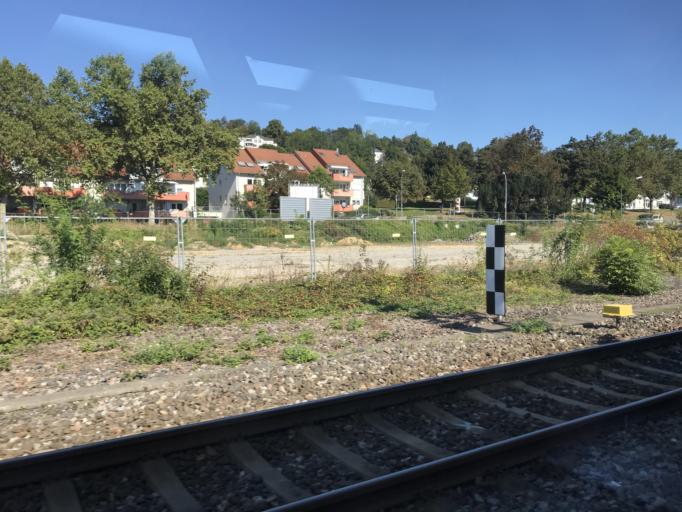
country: DE
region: Baden-Wuerttemberg
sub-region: Karlsruhe Region
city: Pforzheim
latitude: 48.8950
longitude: 8.6854
